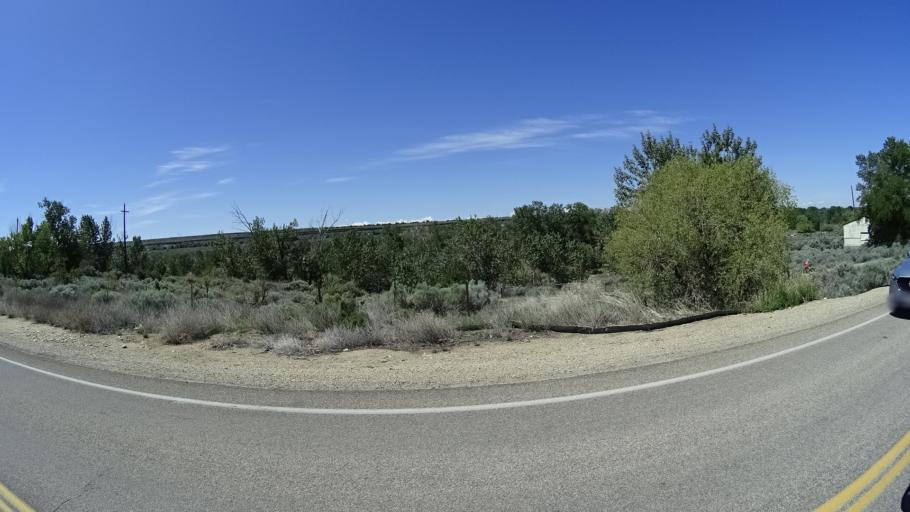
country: US
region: Idaho
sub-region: Ada County
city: Boise
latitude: 43.5615
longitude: -116.1045
